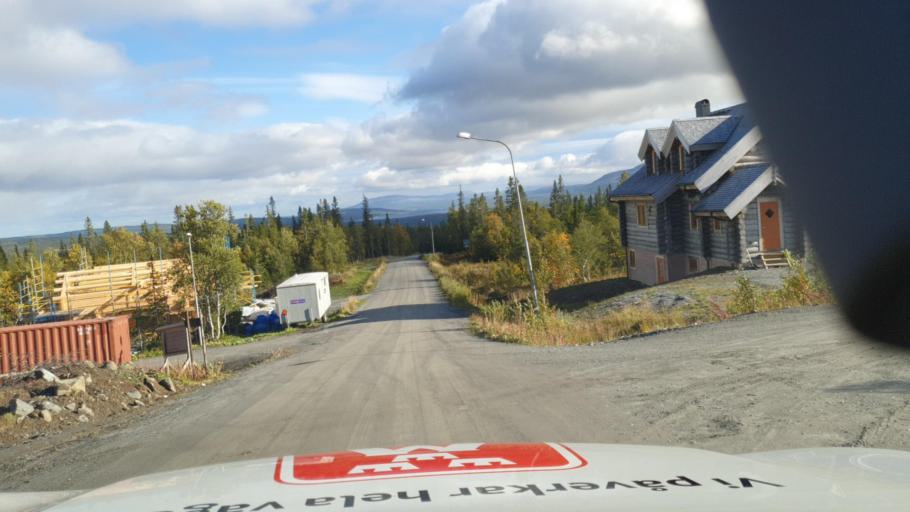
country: SE
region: Jaemtland
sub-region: Are Kommun
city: Are
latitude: 63.2649
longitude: 13.1654
